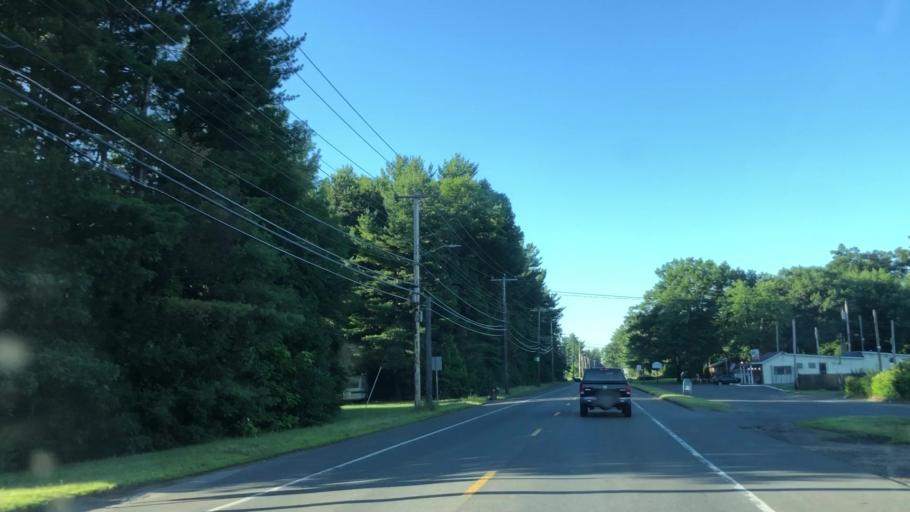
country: US
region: Massachusetts
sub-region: Hampden County
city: Westfield
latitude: 42.1702
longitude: -72.7269
